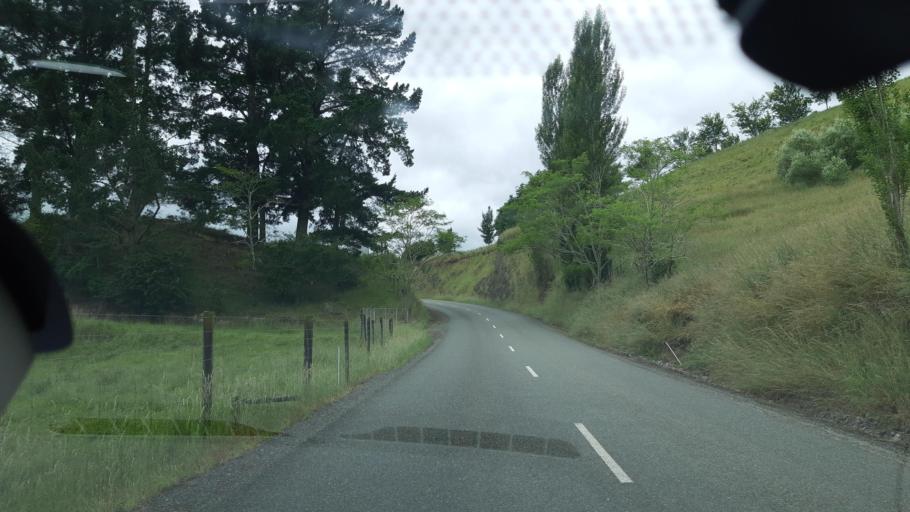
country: NZ
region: Tasman
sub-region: Tasman District
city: Wakefield
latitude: -41.4490
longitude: 173.0539
